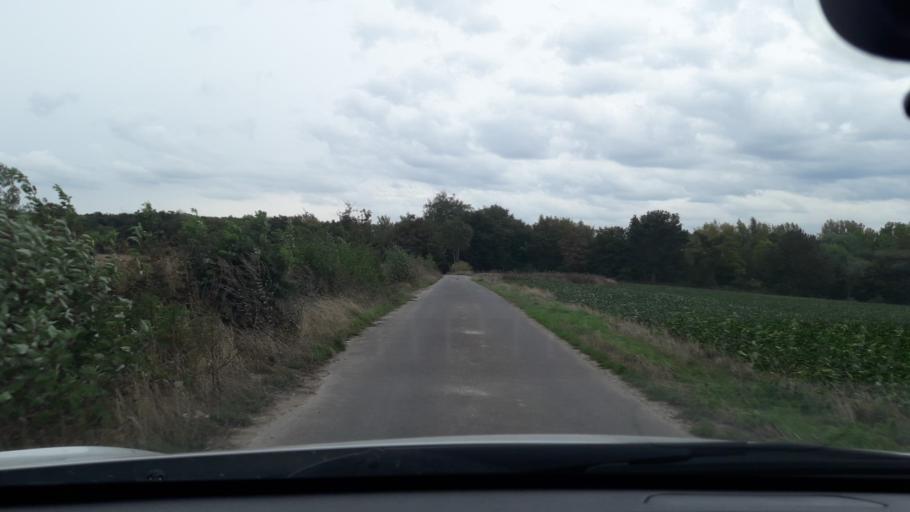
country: DE
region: Lower Saxony
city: Liebenburg
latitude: 52.0540
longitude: 10.4555
